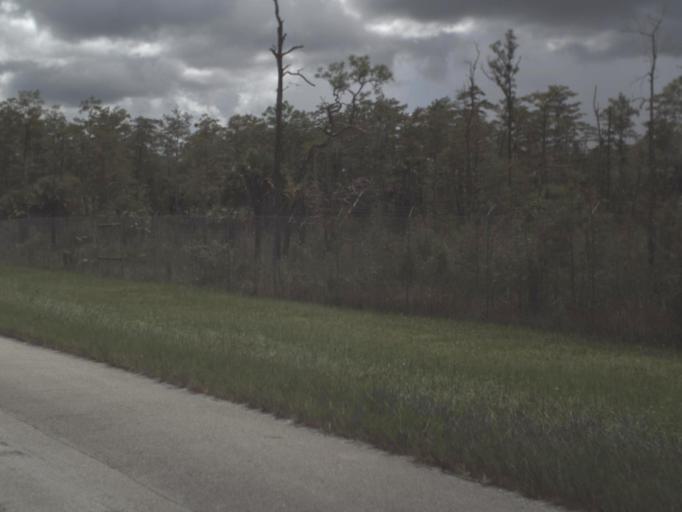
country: US
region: Florida
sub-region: Collier County
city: Immokalee
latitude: 26.1551
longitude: -81.2864
